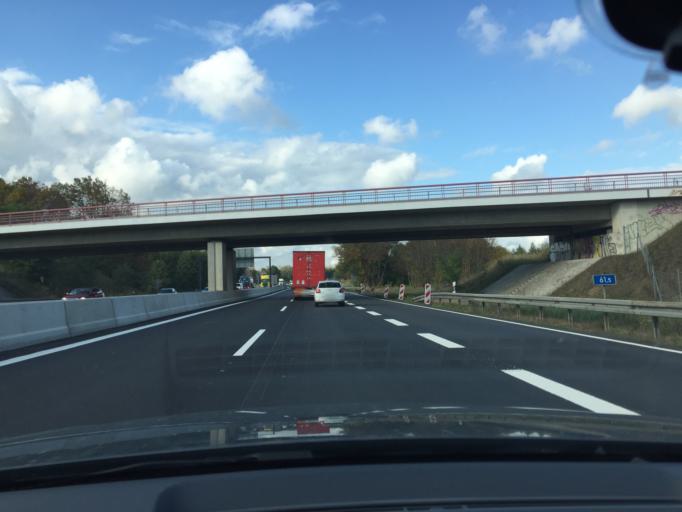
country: DE
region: Brandenburg
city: Lubbenau
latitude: 51.8493
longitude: 13.9131
